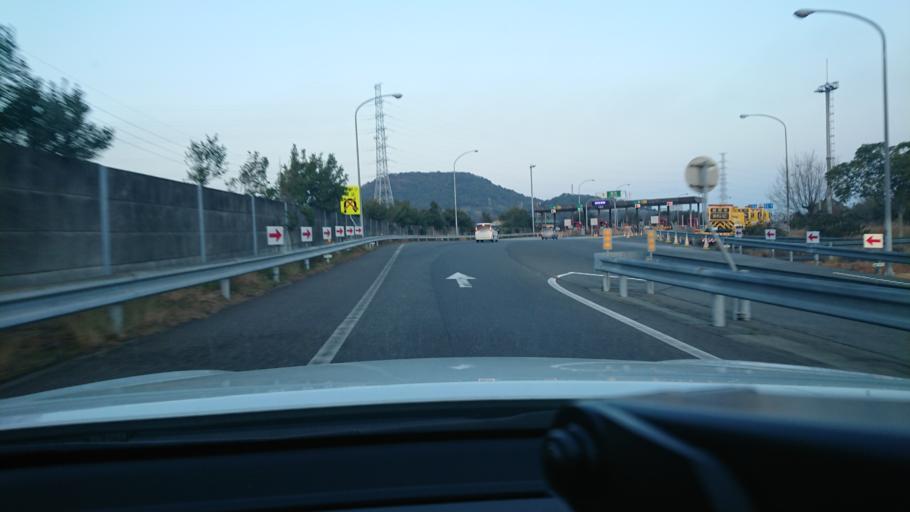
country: JP
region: Kagawa
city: Sakaidecho
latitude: 34.2956
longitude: 133.8434
